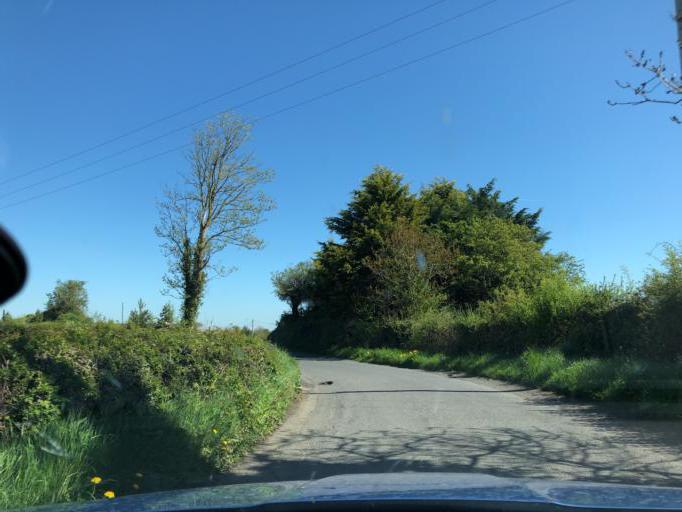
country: IE
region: Connaught
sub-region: County Galway
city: Portumna
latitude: 53.1551
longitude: -8.2949
